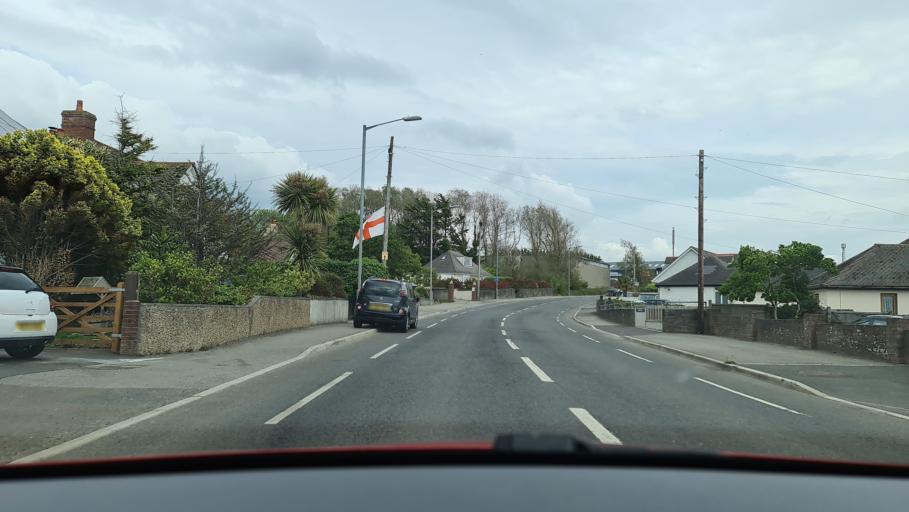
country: GB
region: England
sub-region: Cornwall
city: Bude
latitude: 50.8209
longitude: -4.5355
